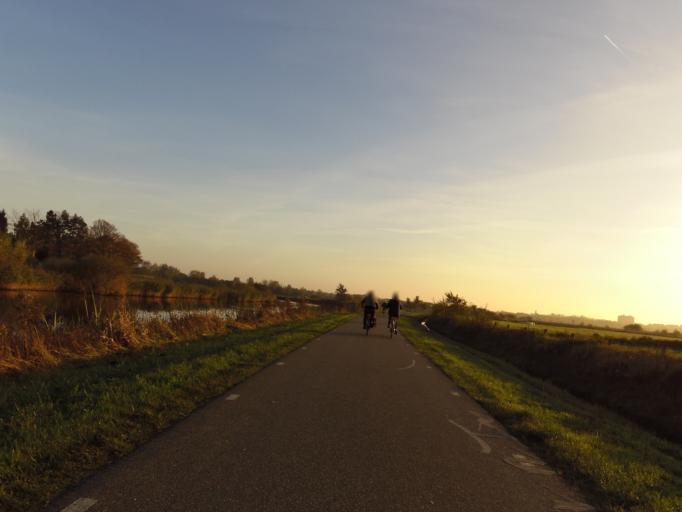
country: NL
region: North Brabant
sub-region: Gemeente 's-Hertogenbosch
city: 's-Hertogenbosch
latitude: 51.6813
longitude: 5.3089
